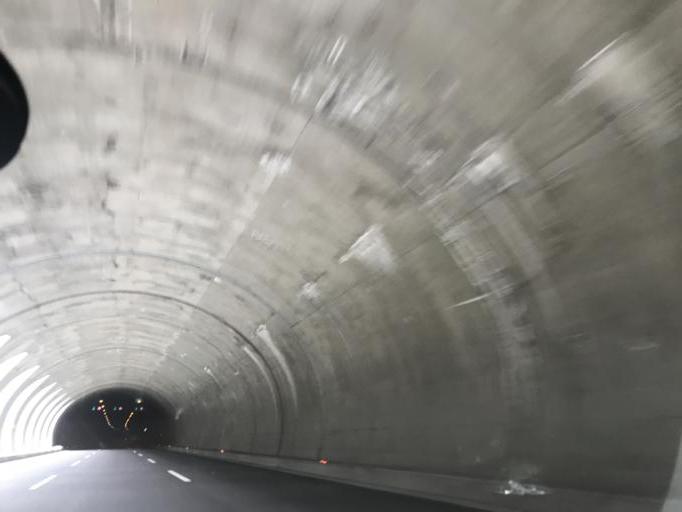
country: TR
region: Nigde
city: Ciftehan
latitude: 37.4941
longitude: 34.8355
